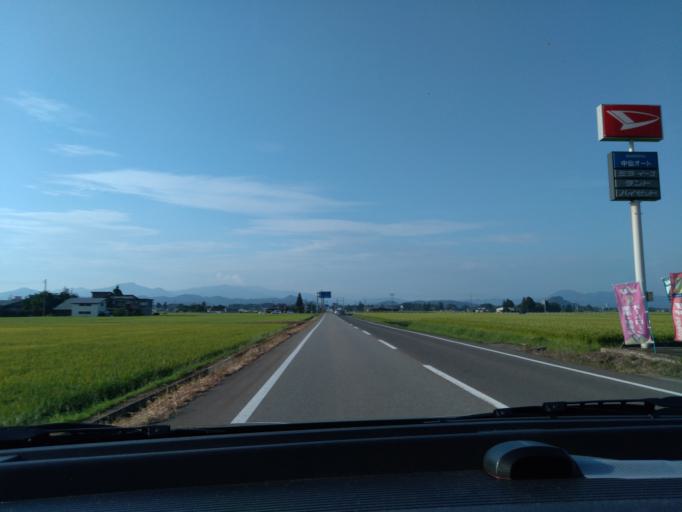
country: JP
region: Akita
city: Kakunodatemachi
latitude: 39.5437
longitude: 140.5579
